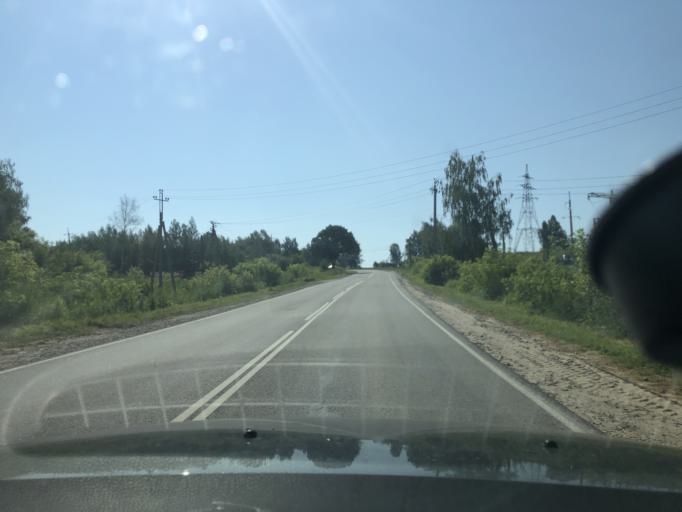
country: RU
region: Tula
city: Dubna
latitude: 54.1489
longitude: 36.9707
